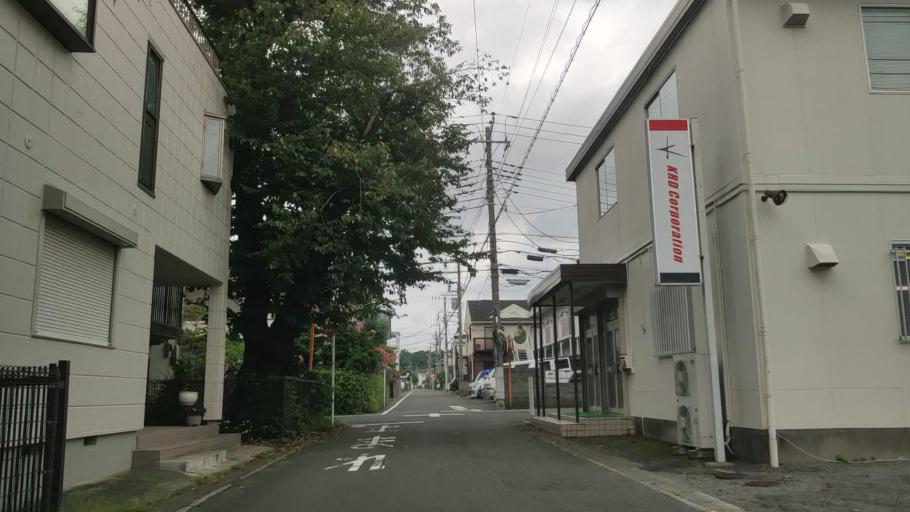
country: JP
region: Kanagawa
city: Minami-rinkan
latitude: 35.5099
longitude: 139.4472
